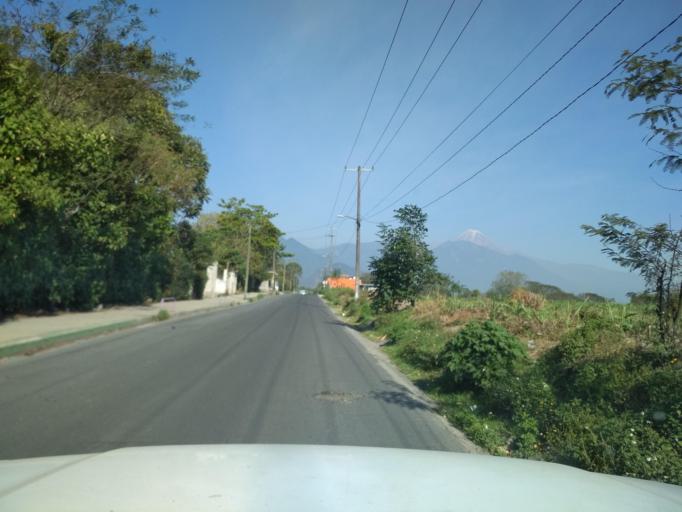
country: MX
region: Veracruz
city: Jalapilla
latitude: 18.8177
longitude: -97.0775
